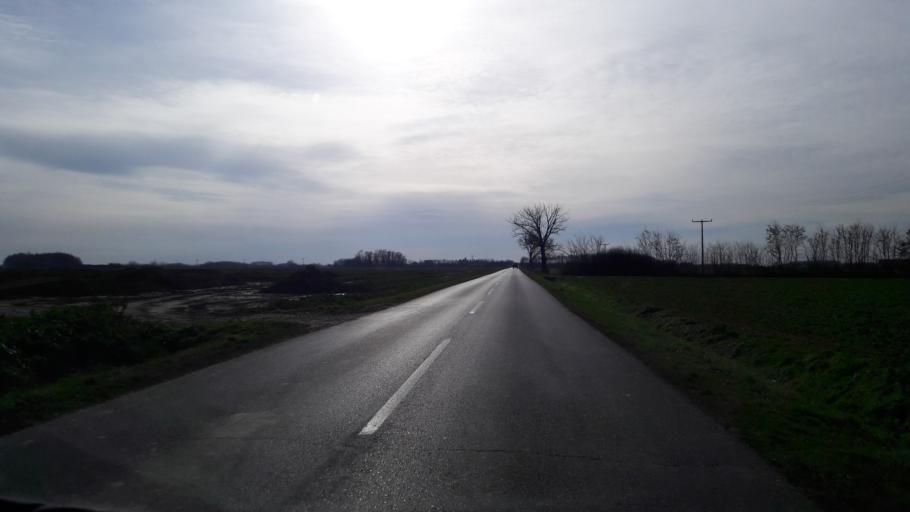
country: HR
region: Osjecko-Baranjska
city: Semeljci
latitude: 45.3230
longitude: 18.5574
